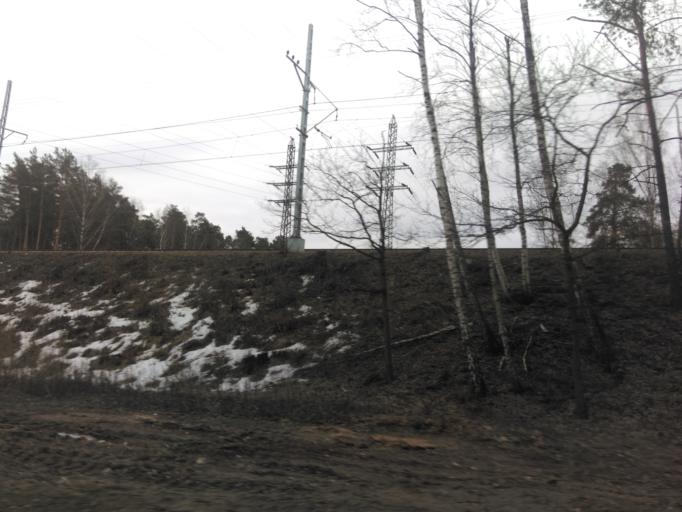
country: RU
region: Moskovskaya
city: Nemchinovka
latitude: 55.7499
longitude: 37.3290
